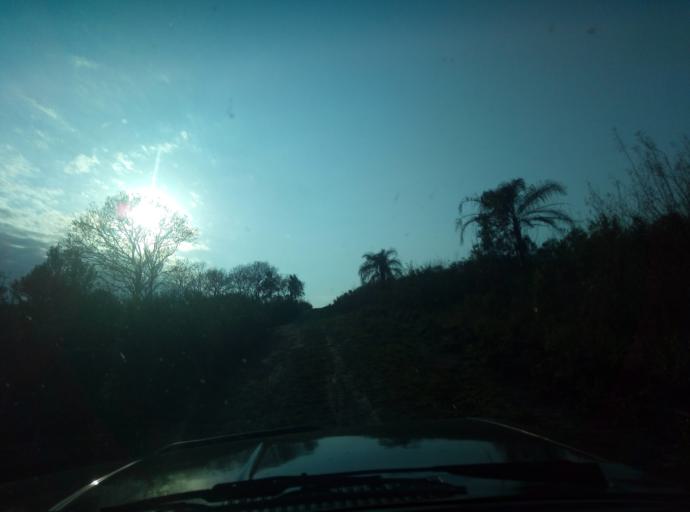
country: PY
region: Caaguazu
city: Doctor Cecilio Baez
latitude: -25.1988
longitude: -56.1243
